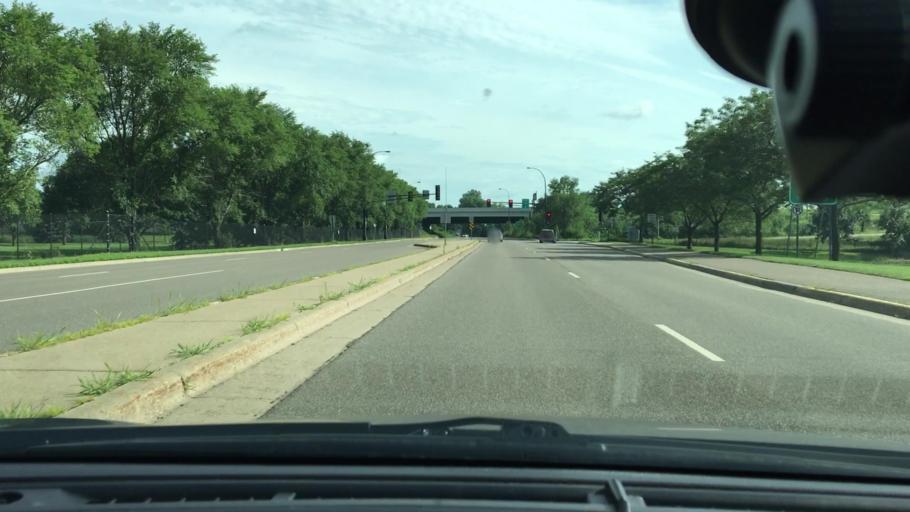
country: US
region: Minnesota
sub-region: Hennepin County
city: Saint Louis Park
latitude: 44.9766
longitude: -93.3908
